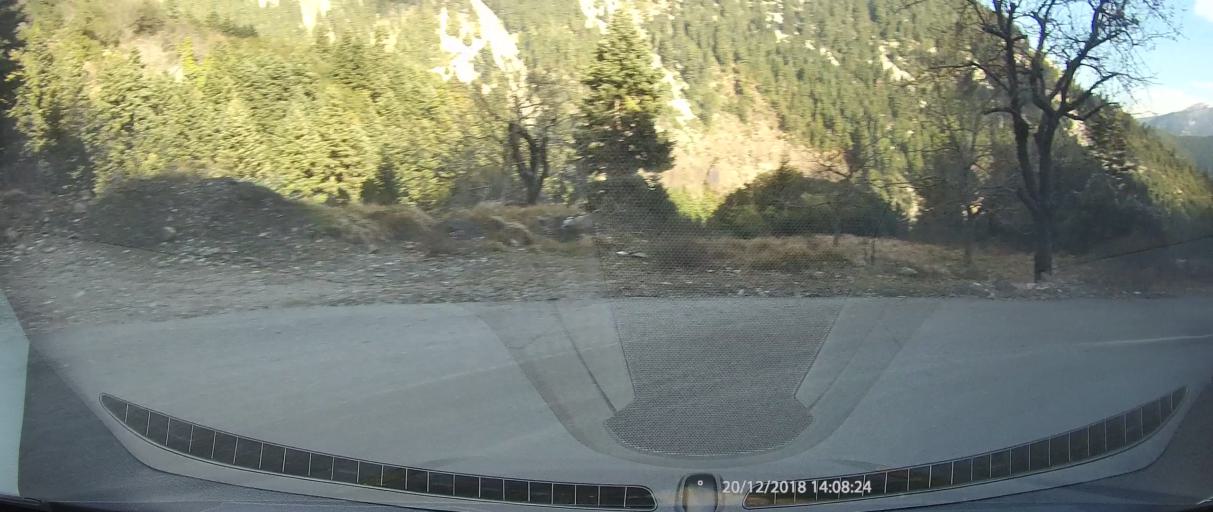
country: GR
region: West Greece
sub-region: Nomos Aitolias kai Akarnanias
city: Thermo
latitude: 38.7554
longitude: 21.6455
